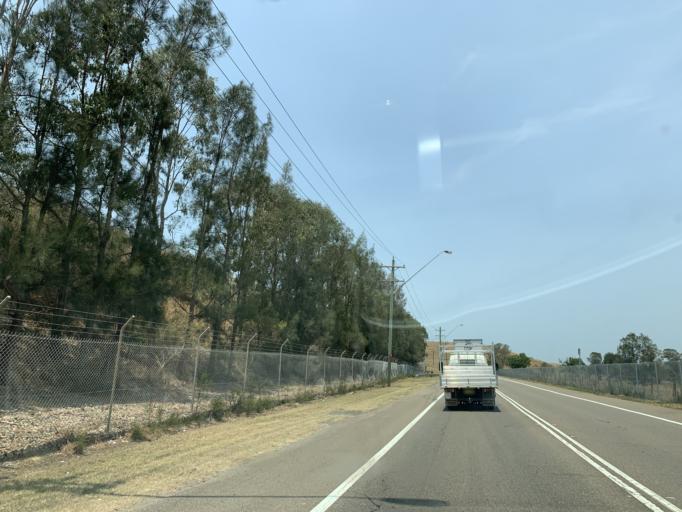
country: AU
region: New South Wales
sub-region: Blacktown
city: Doonside
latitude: -33.8058
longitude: 150.8642
